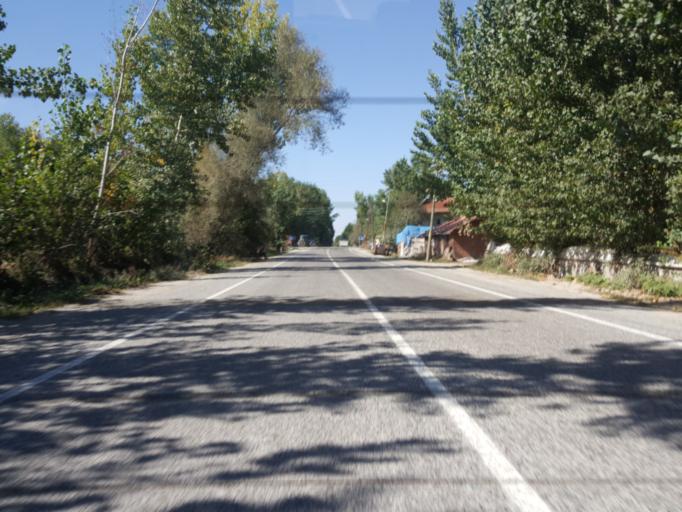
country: TR
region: Tokat
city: Pazar
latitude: 40.2701
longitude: 36.2420
